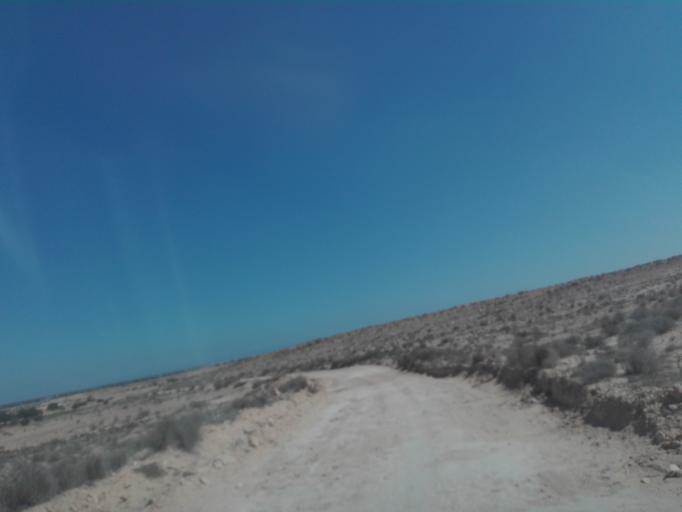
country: TN
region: Qabis
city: Gabes
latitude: 33.8481
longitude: 9.9966
